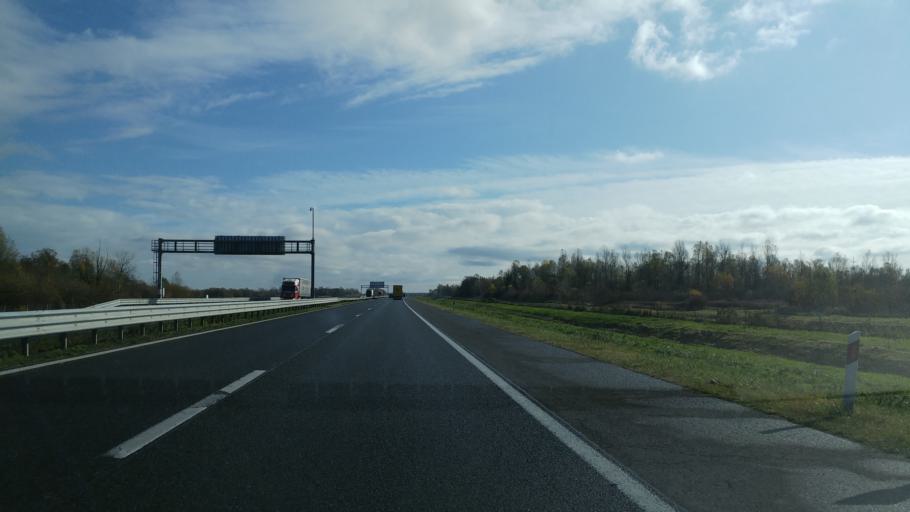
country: HR
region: Grad Zagreb
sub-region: Sesvete
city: Sesvete
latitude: 45.7839
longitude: 16.1851
